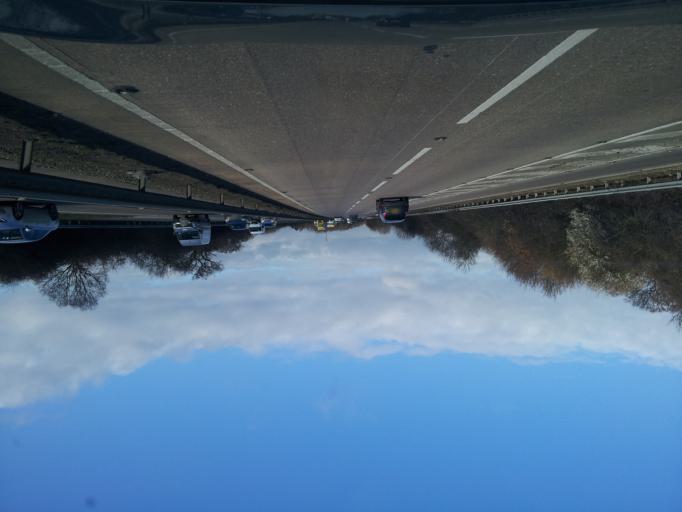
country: GB
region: England
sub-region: Suffolk
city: Bramford
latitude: 52.0651
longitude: 1.1088
